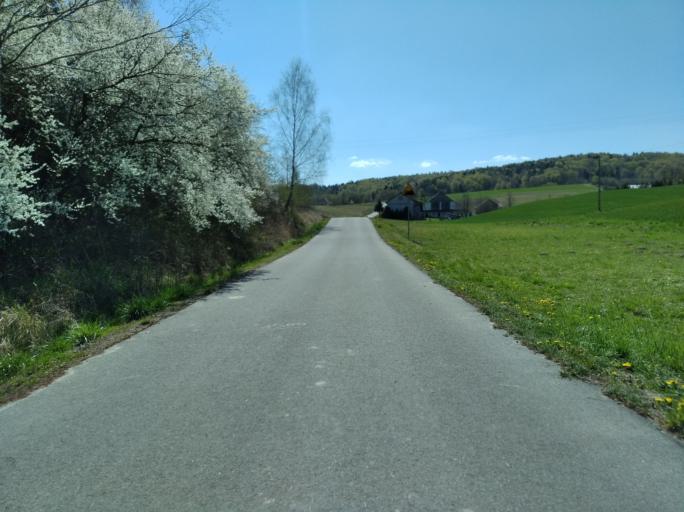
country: PL
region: Subcarpathian Voivodeship
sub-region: Powiat strzyzowski
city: Wisniowa
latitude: 49.9043
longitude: 21.6820
